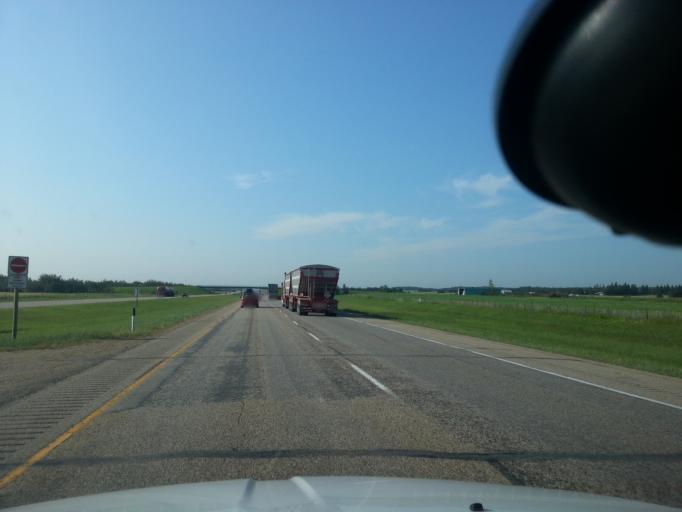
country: CA
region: Alberta
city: Millet
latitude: 52.9208
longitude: -113.6441
